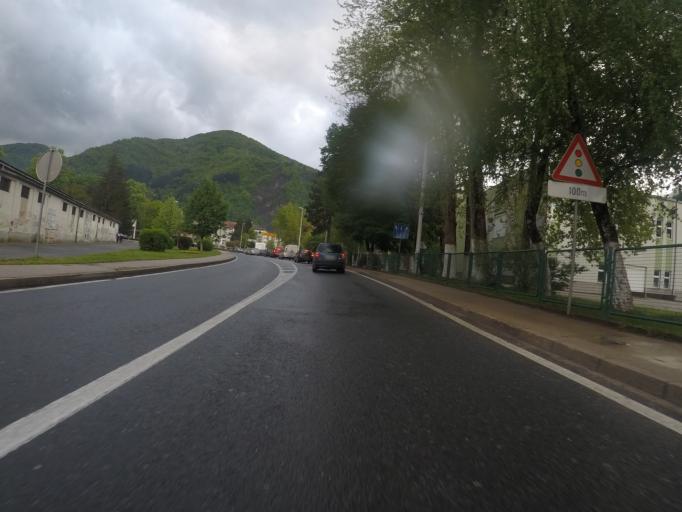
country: BA
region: Federation of Bosnia and Herzegovina
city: Jablanica
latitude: 43.6595
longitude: 17.7627
